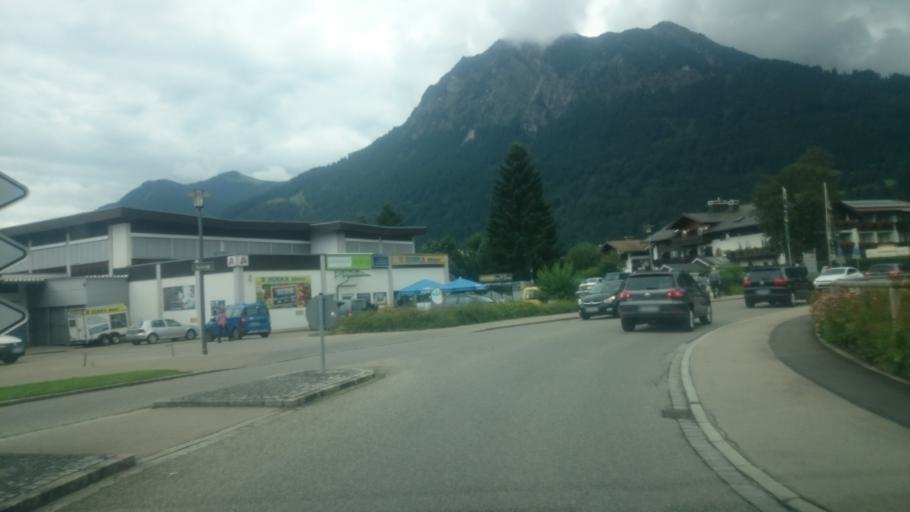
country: DE
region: Bavaria
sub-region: Swabia
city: Oberstdorf
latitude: 47.4123
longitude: 10.2757
